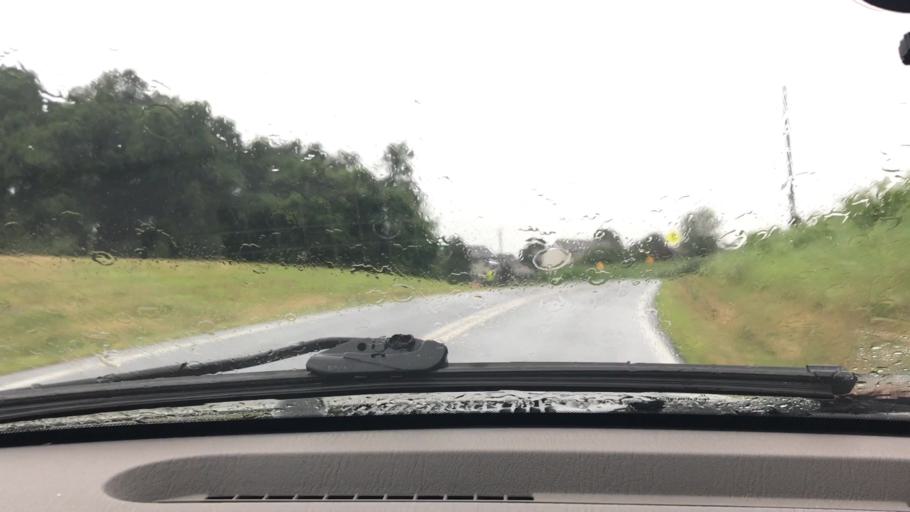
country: US
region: Pennsylvania
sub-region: Lancaster County
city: Elizabethtown
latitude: 40.1308
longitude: -76.6143
